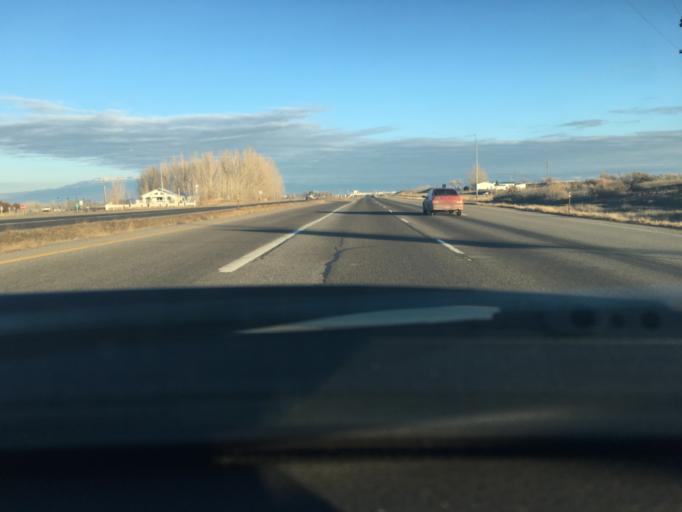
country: US
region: Colorado
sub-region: Montrose County
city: Olathe
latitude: 38.5969
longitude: -107.9729
